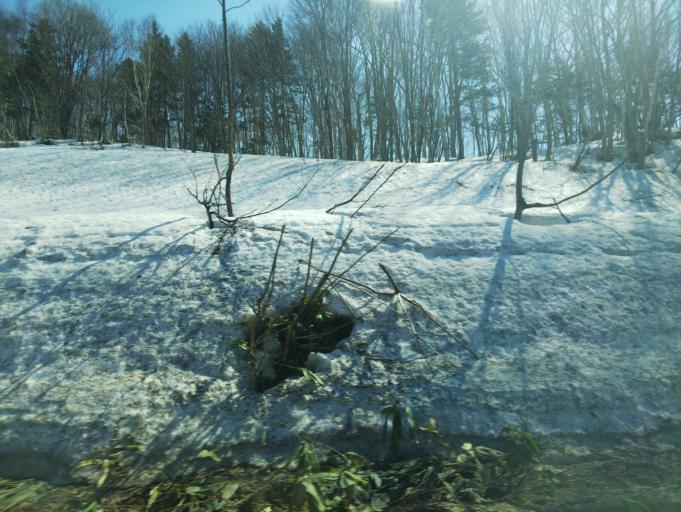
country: JP
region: Hokkaido
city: Nayoro
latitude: 44.7013
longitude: 142.2733
